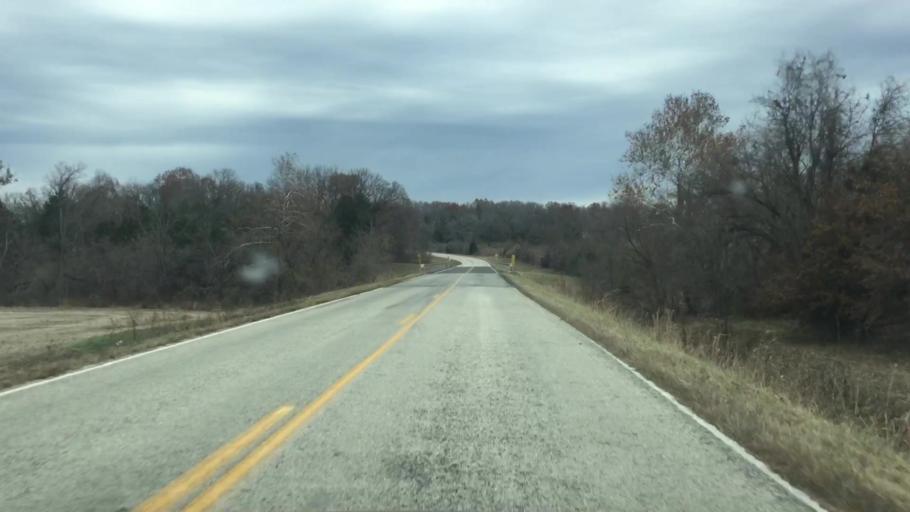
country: US
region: Missouri
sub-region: Saint Clair County
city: Osceola
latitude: 37.9850
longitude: -93.6118
